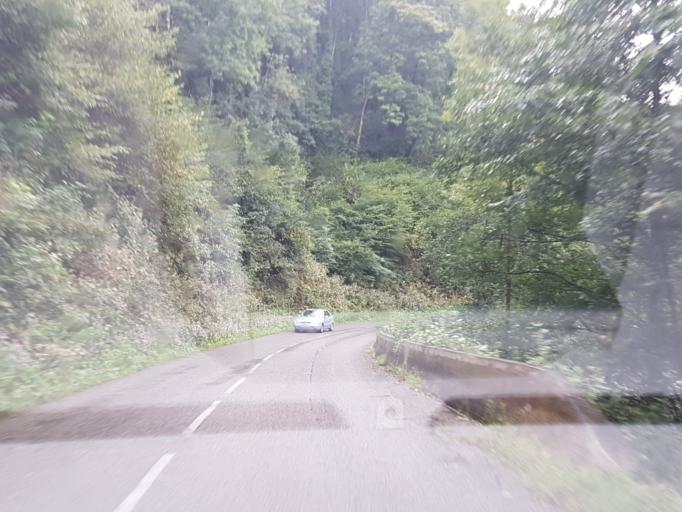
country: FR
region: Midi-Pyrenees
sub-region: Departement de l'Ariege
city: Saint-Girons
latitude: 42.9010
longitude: 1.2260
